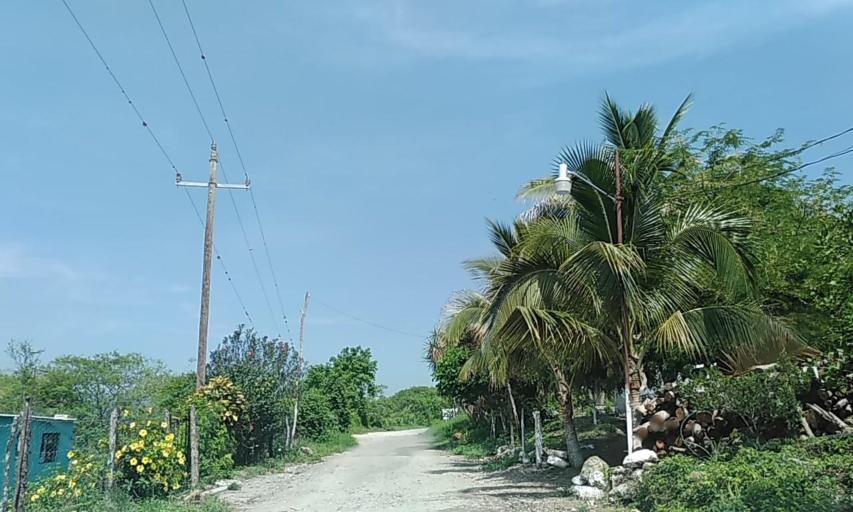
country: MX
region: Veracruz
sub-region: Emiliano Zapata
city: Plan del Rio
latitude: 19.4519
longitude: -96.6801
